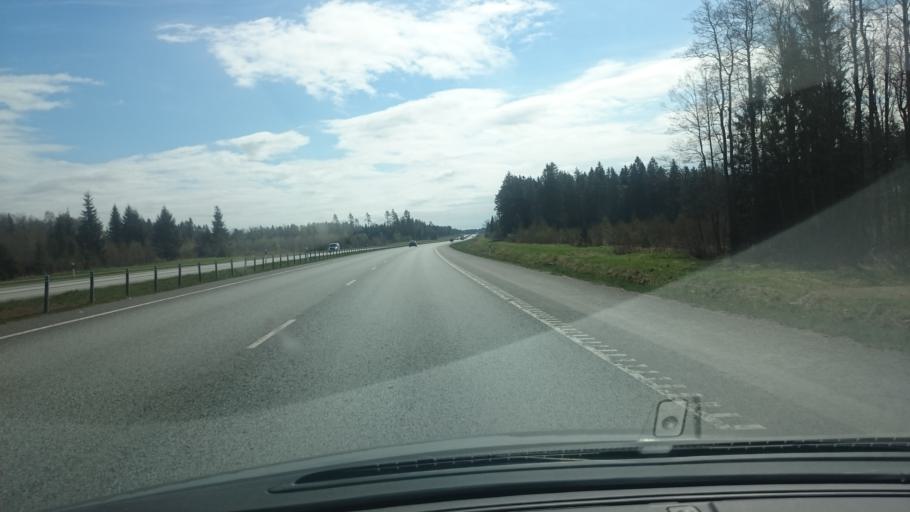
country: EE
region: Laeaene-Virumaa
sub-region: Kadrina vald
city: Kadrina
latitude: 59.4608
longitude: 26.0289
